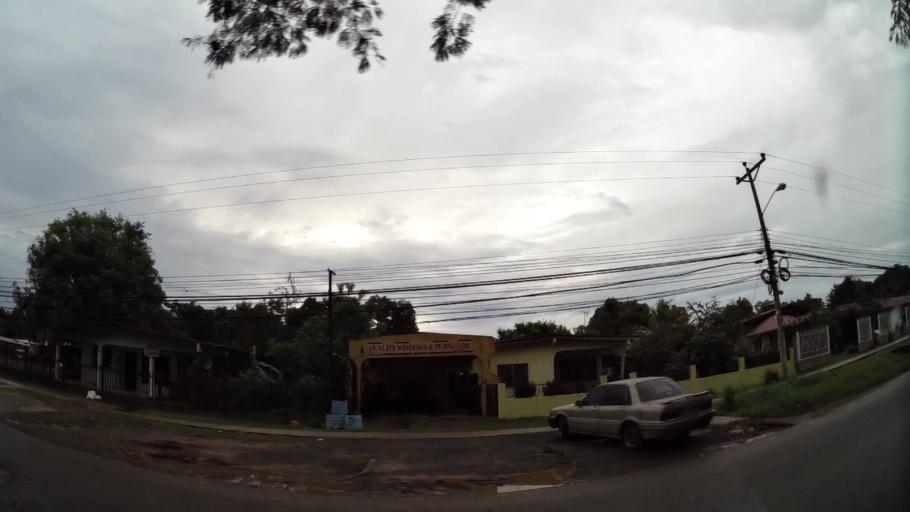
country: PA
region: Veraguas
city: Santiago de Veraguas
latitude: 8.1166
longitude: -80.9675
